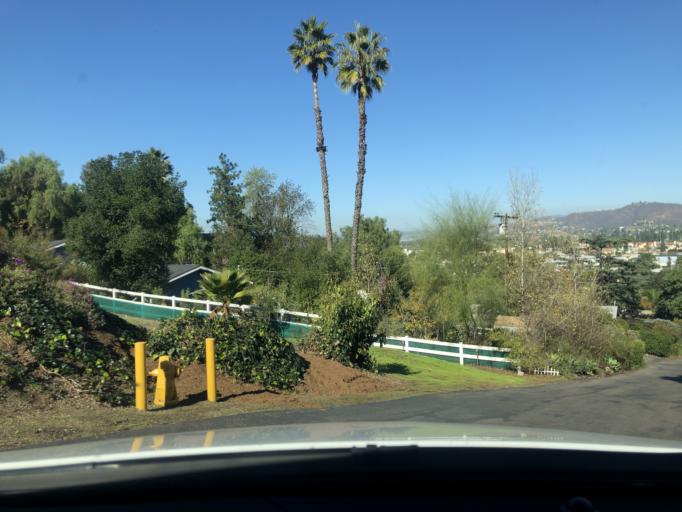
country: US
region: California
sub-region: San Diego County
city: El Cajon
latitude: 32.7848
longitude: -116.9428
